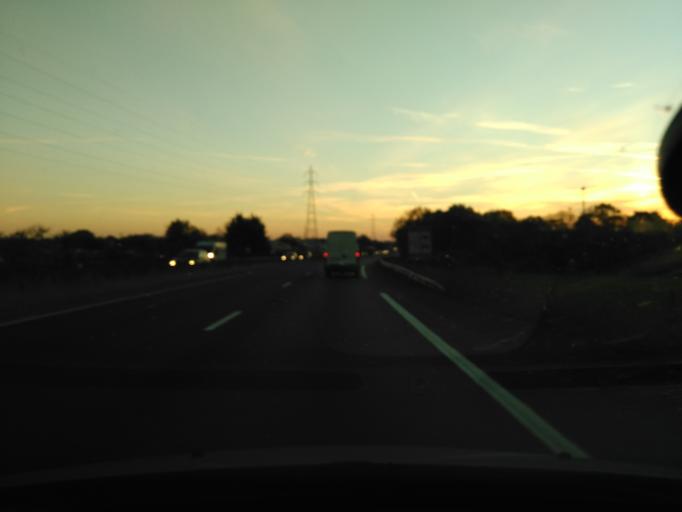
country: FR
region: Poitou-Charentes
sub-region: Departement de la Charente-Maritime
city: Lagord
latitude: 46.1812
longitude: -1.1450
